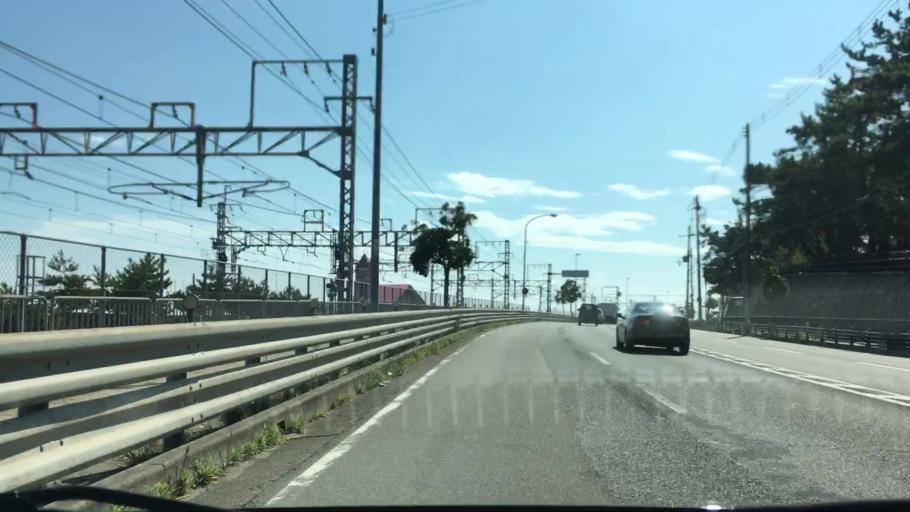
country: JP
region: Hyogo
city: Kobe
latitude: 34.6382
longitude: 135.1027
